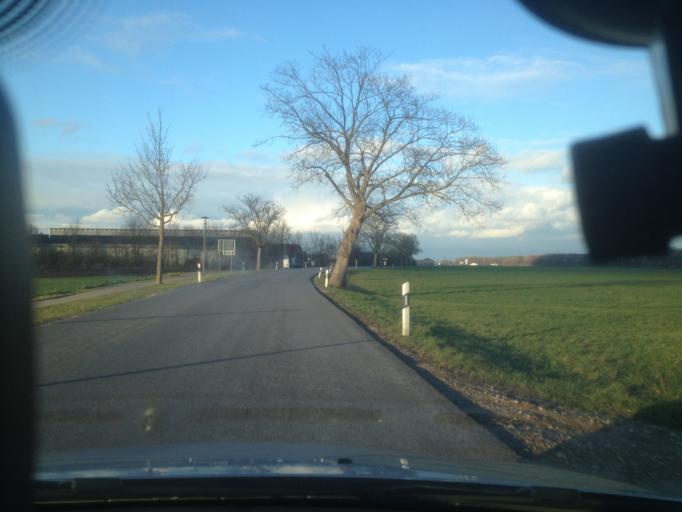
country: DE
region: Bavaria
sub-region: Upper Bavaria
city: Prittriching
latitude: 48.2093
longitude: 10.9310
